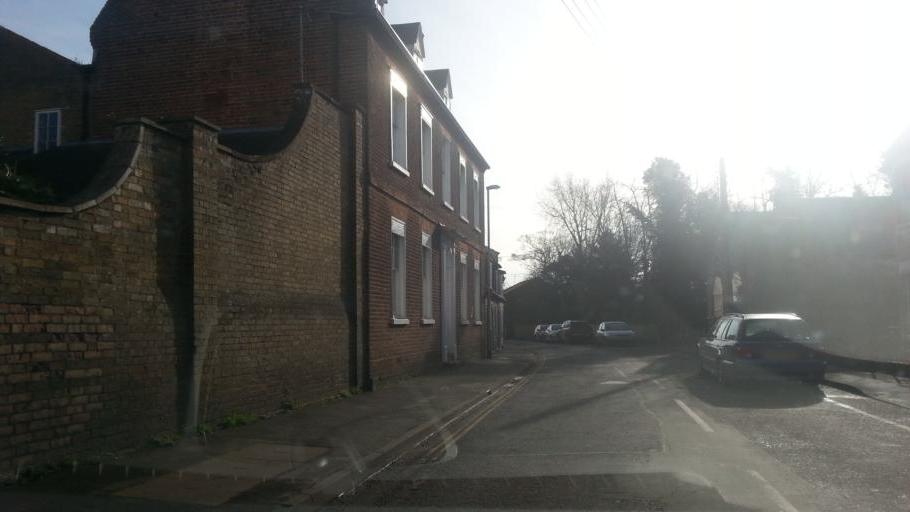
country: GB
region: England
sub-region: Cambridgeshire
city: Somersham
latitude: 52.3820
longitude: 0.0002
